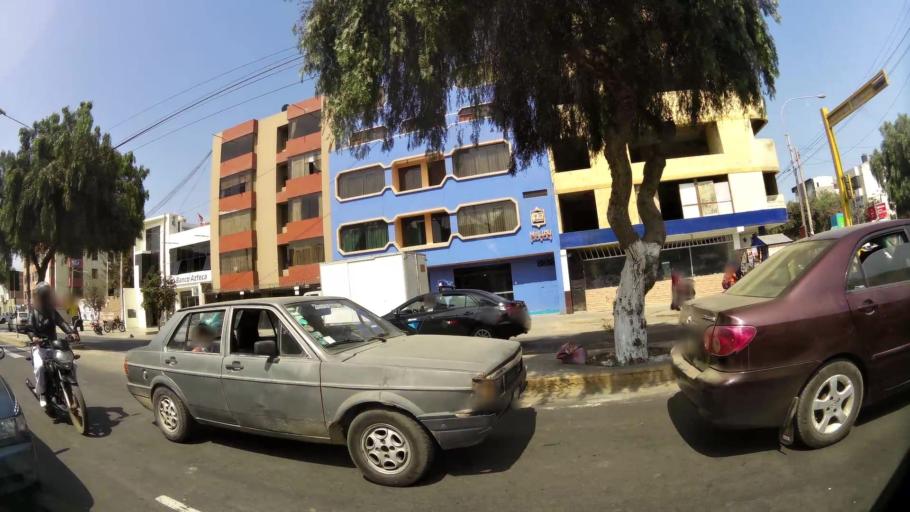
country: PE
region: La Libertad
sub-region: Provincia de Trujillo
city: Buenos Aires
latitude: -8.1273
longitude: -79.0413
